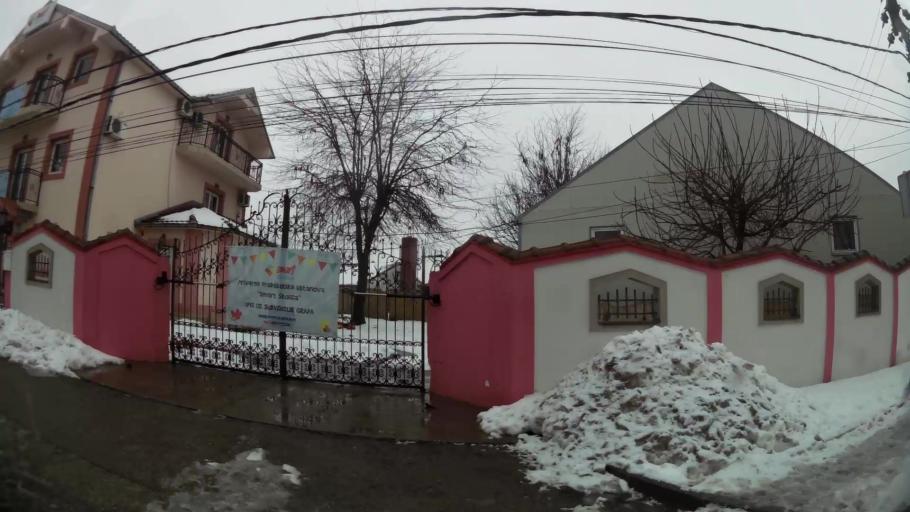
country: RS
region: Central Serbia
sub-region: Belgrade
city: Zemun
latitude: 44.8479
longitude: 20.3551
